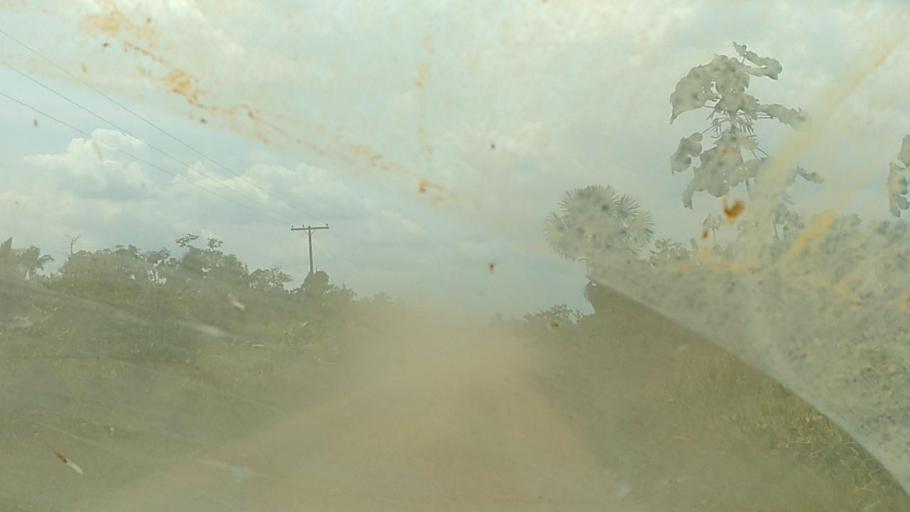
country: BR
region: Rondonia
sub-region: Porto Velho
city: Porto Velho
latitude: -8.9470
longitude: -64.3101
